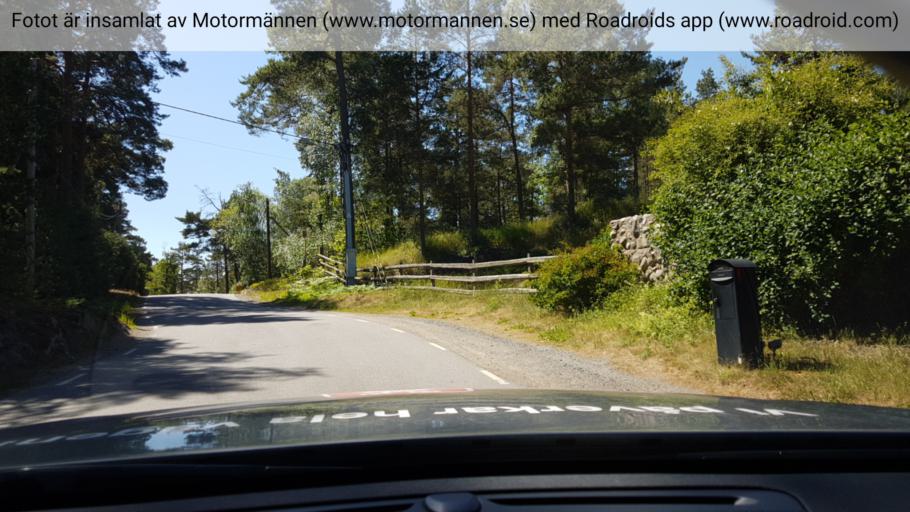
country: SE
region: Stockholm
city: Dalaro
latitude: 59.1439
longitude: 18.4343
